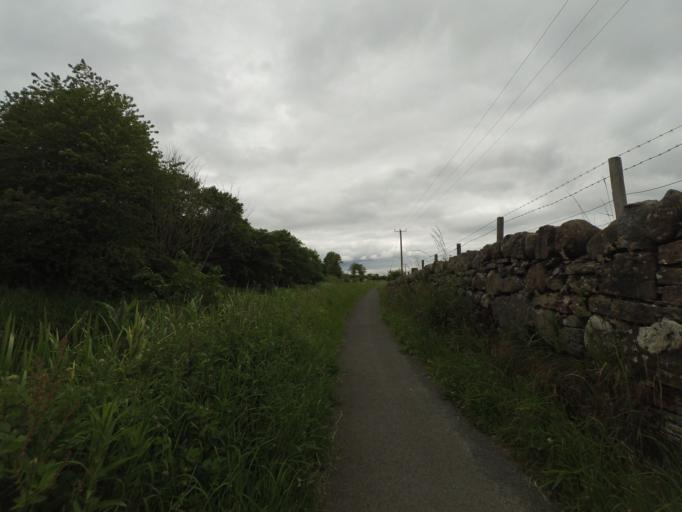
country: GB
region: Scotland
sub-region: West Lothian
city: Linlithgow
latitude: 55.9768
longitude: -3.5449
